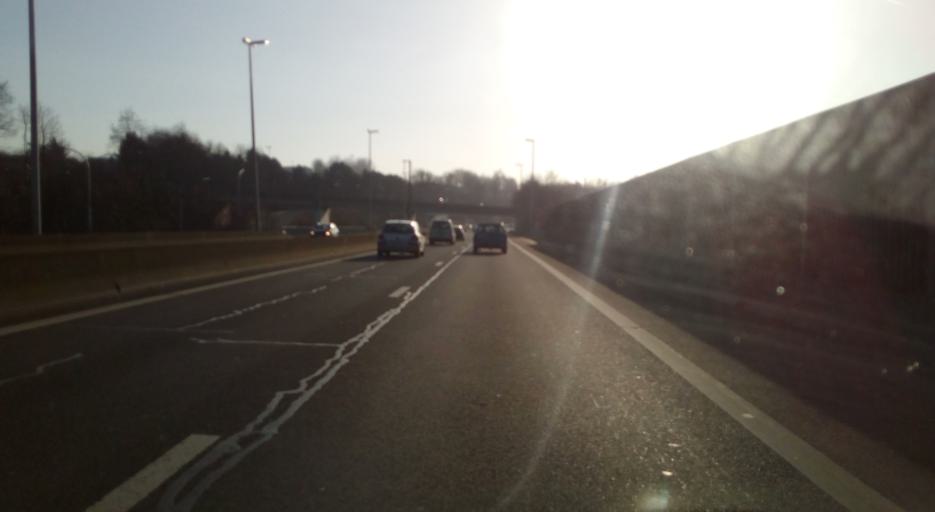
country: BE
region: Wallonia
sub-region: Province du Hainaut
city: Charleroi
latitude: 50.4305
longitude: 4.4528
